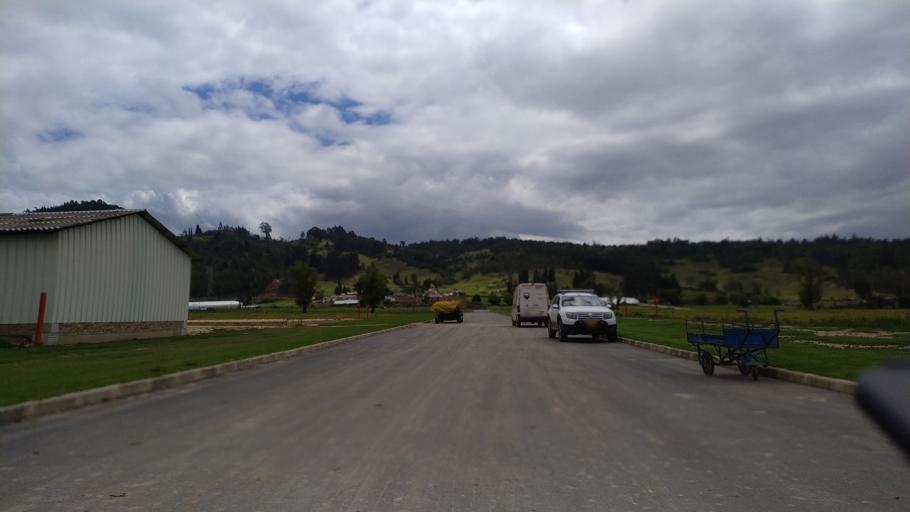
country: CO
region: Boyaca
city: Duitama
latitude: 5.7978
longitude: -73.0672
